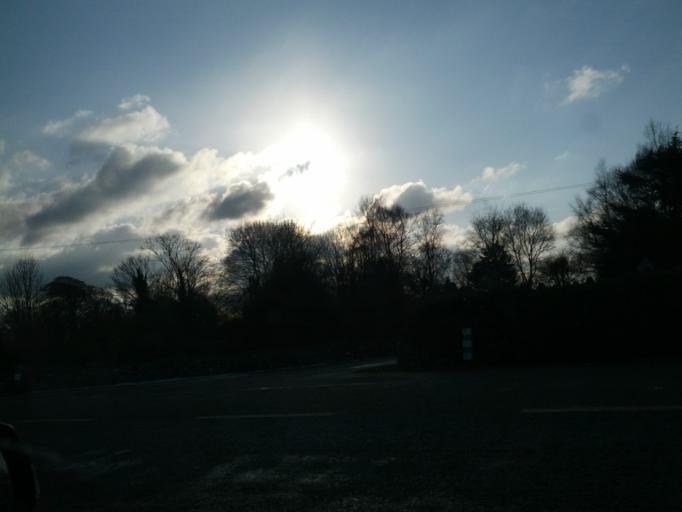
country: IE
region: Connaught
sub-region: County Galway
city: Gort
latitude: 53.1526
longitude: -8.8057
